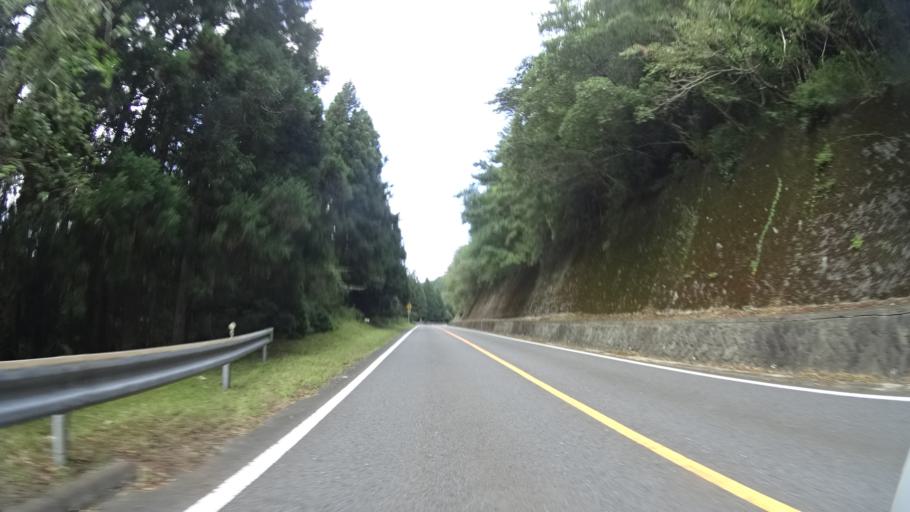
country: JP
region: Oita
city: Tsukawaki
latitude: 33.2471
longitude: 131.2921
